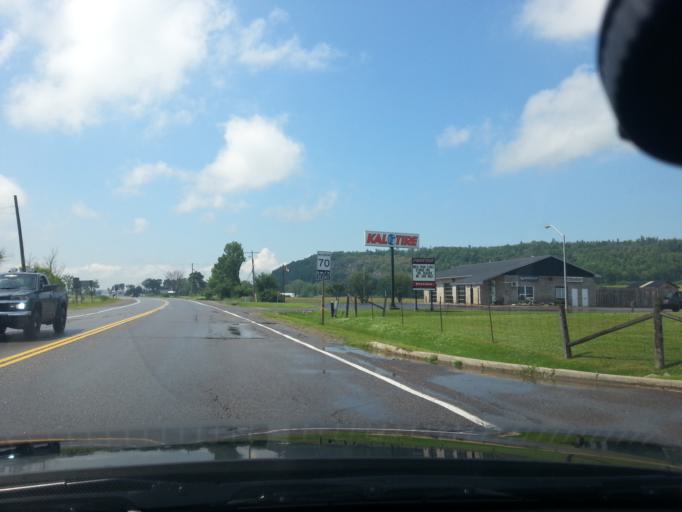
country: CA
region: Ontario
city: Renfrew
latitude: 45.4827
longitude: -76.7039
